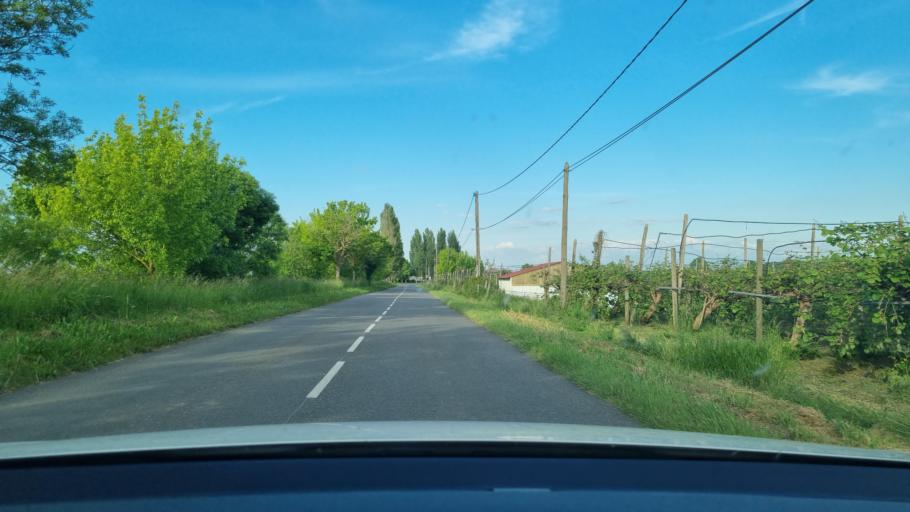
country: FR
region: Aquitaine
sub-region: Departement des Pyrenees-Atlantiques
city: Bardos
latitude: 43.5297
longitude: -1.2176
